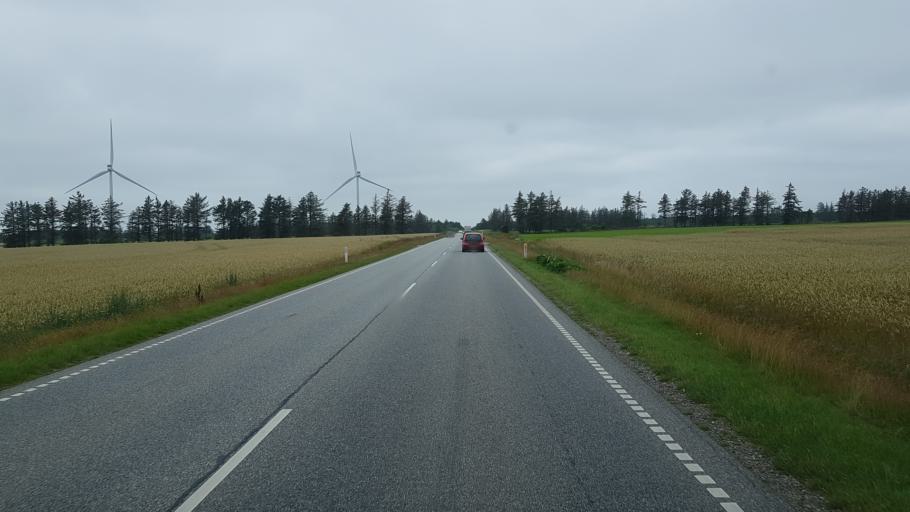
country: DK
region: Central Jutland
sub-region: Lemvig Kommune
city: Lemvig
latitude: 56.4440
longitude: 8.3604
